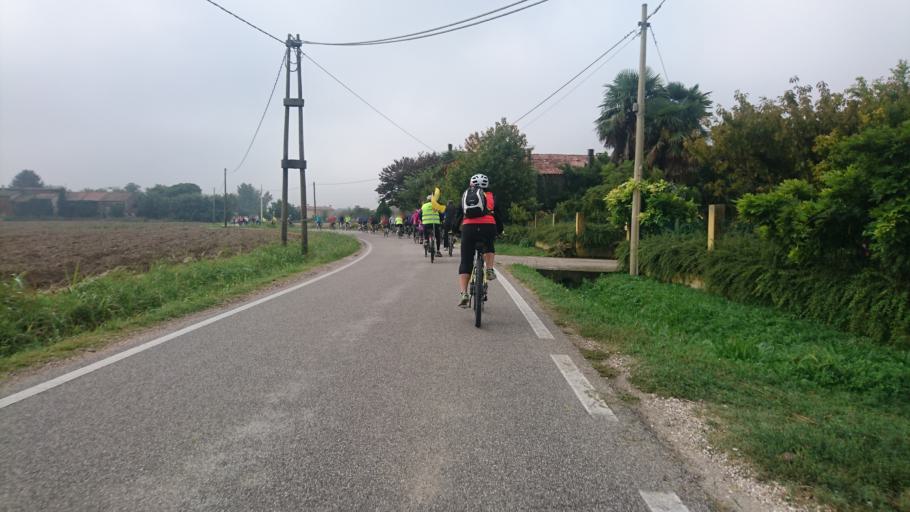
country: IT
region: Veneto
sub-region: Provincia di Padova
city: Monselice
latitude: 45.2184
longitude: 11.7723
